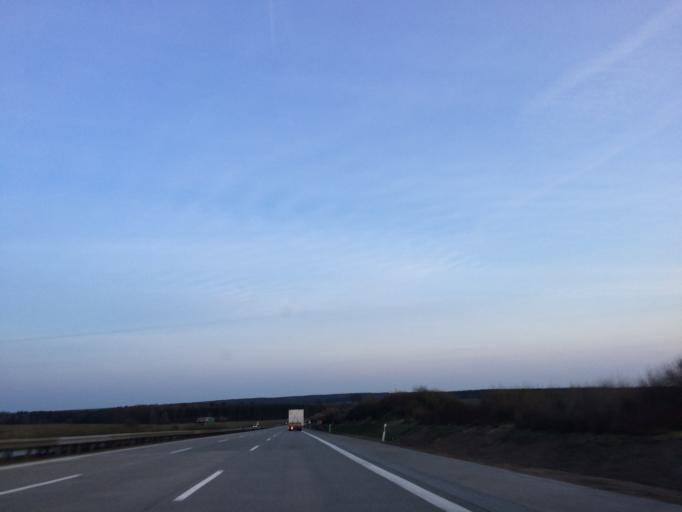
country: DE
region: Thuringia
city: Tautendorf
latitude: 50.8162
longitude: 11.8901
